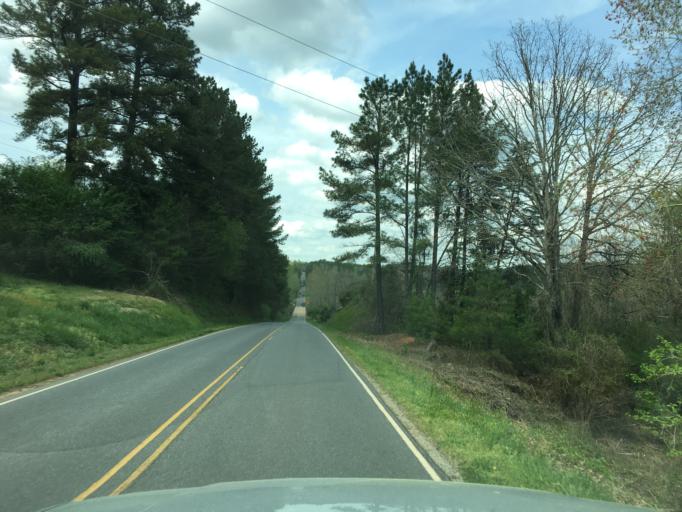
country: US
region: North Carolina
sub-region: Rutherford County
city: Spindale
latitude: 35.2466
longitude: -81.9647
